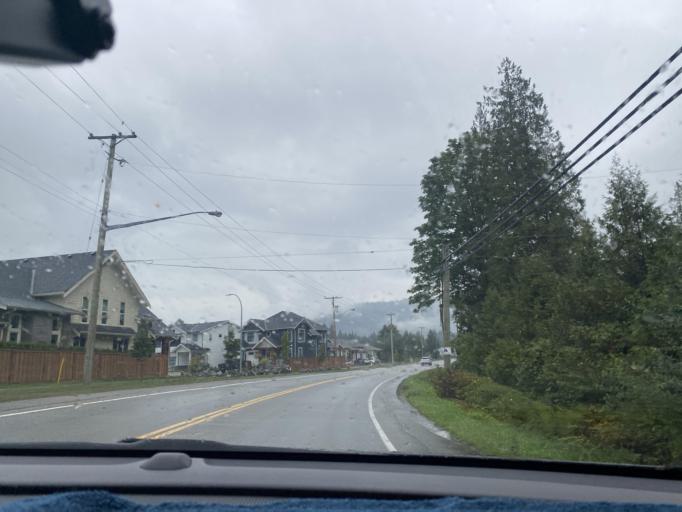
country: CA
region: British Columbia
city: Agassiz
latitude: 49.2935
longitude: -121.7815
